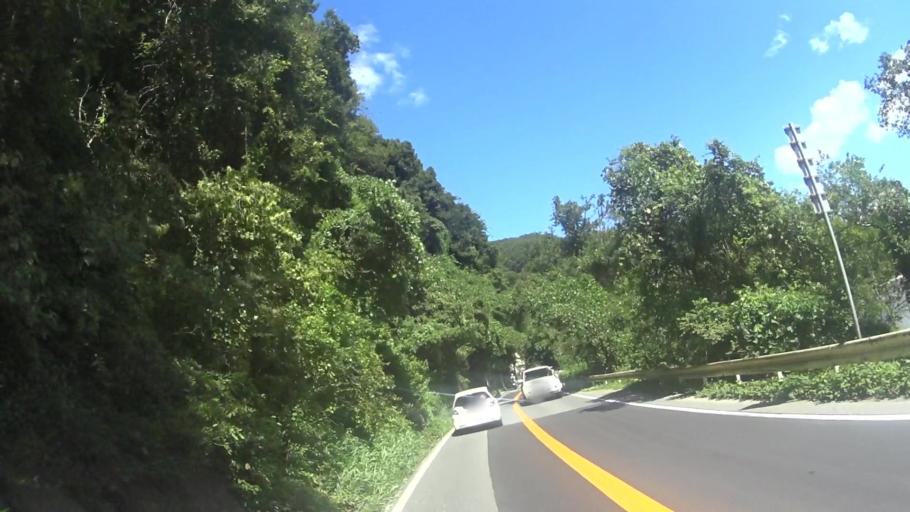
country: JP
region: Nara
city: Nara-shi
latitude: 34.7660
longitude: 135.9013
